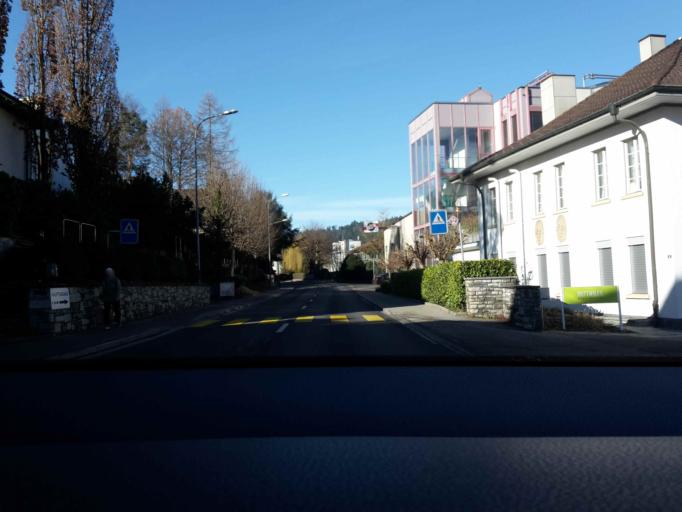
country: CH
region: Bern
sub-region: Oberaargau
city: Huttwil
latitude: 47.1133
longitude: 7.8390
